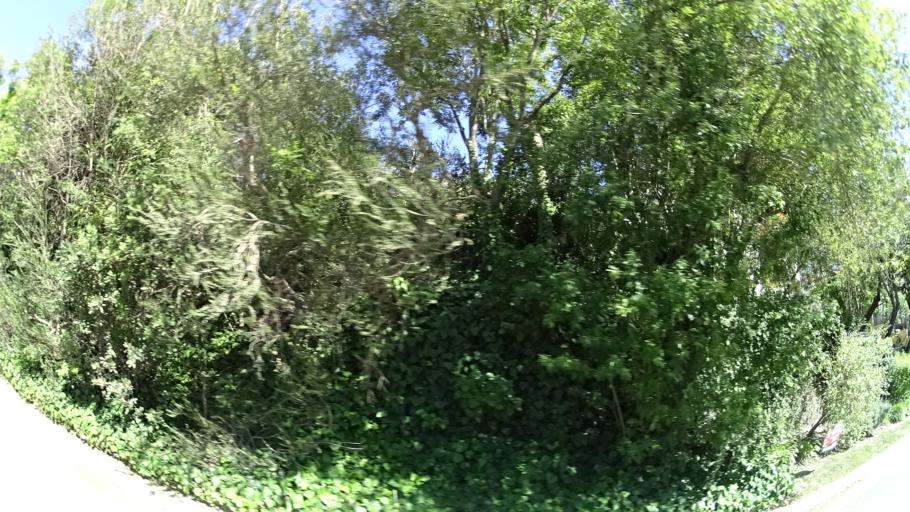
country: US
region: California
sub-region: Los Angeles County
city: Sherman Oaks
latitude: 34.1463
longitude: -118.4531
